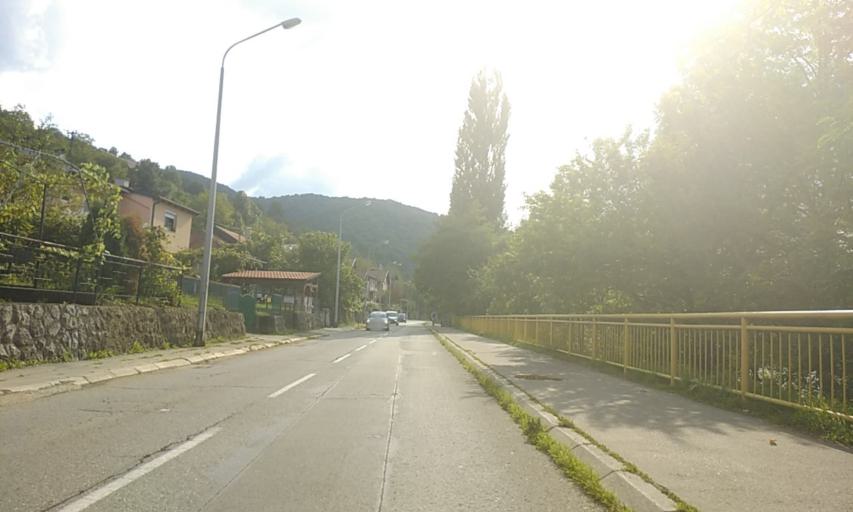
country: BA
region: Republika Srpska
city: Hiseti
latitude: 44.7544
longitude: 17.1791
